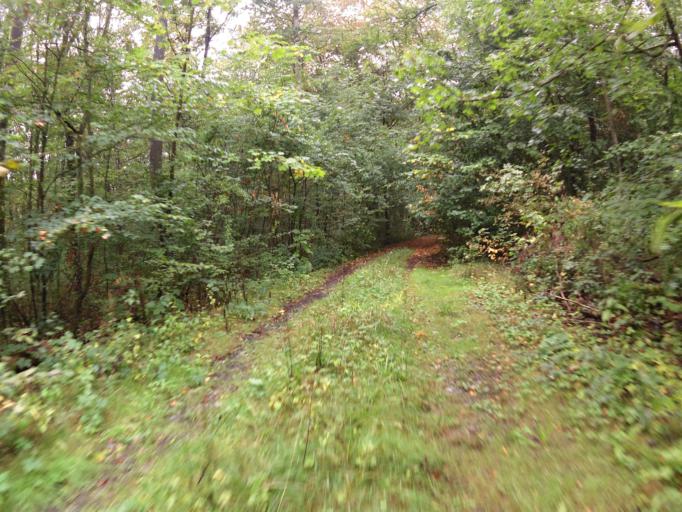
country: DE
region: Bavaria
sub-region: Regierungsbezirk Unterfranken
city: Guntersleben
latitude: 49.8650
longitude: 9.9231
